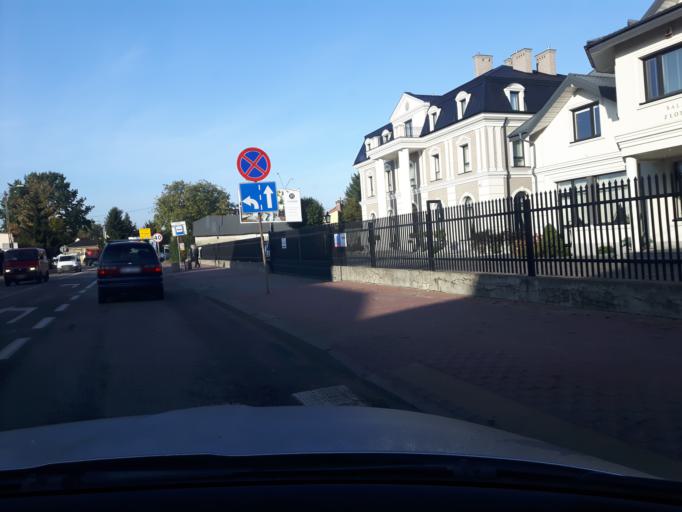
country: PL
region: Masovian Voivodeship
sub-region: Powiat wolominski
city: Zabki
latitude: 52.2887
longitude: 21.1116
